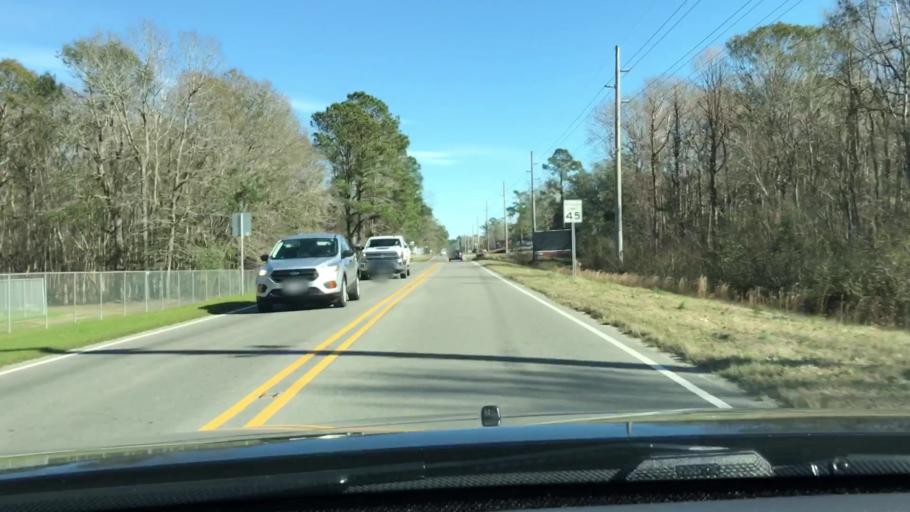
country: US
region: North Carolina
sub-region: Brunswick County
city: Shallotte
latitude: 33.9606
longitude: -78.4097
